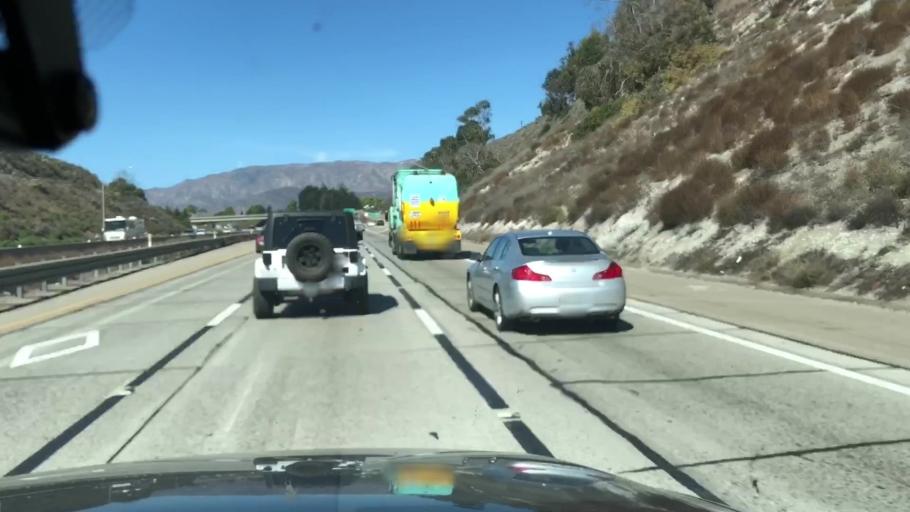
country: US
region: California
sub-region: Santa Barbara County
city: Carpinteria
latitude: 34.3800
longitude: -119.4815
